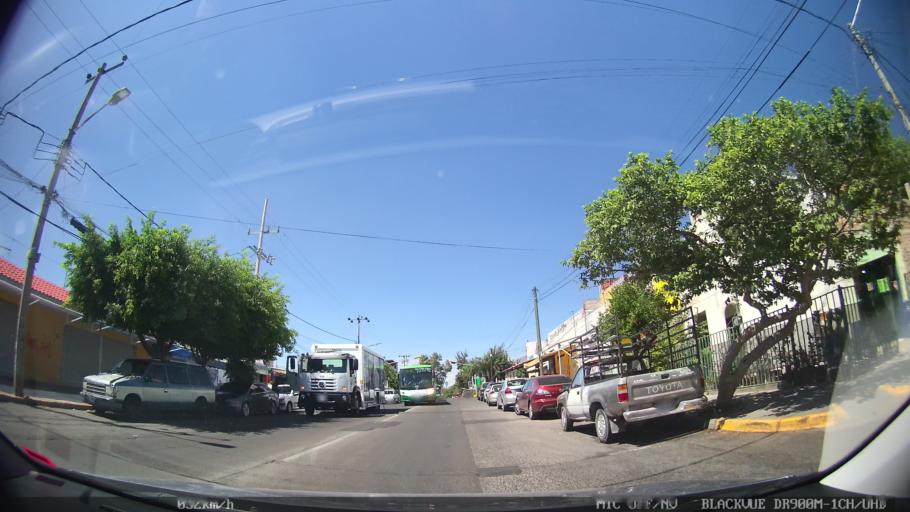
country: MX
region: Jalisco
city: Tlaquepaque
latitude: 20.6896
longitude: -103.2935
